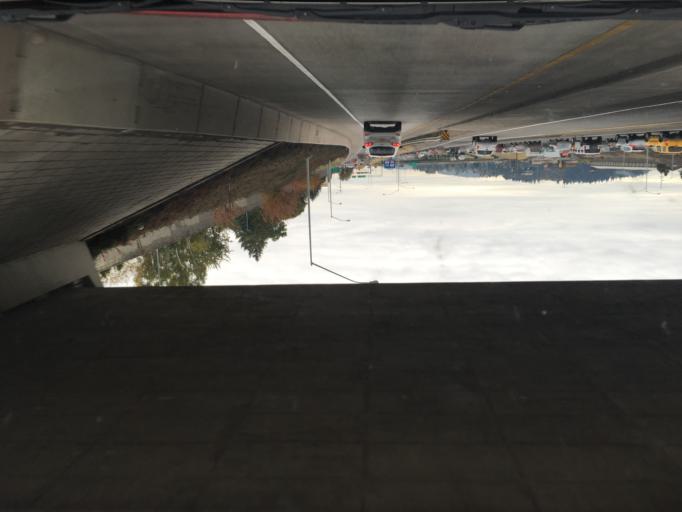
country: US
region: Oregon
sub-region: Multnomah County
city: Lents
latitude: 45.5229
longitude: -122.5658
